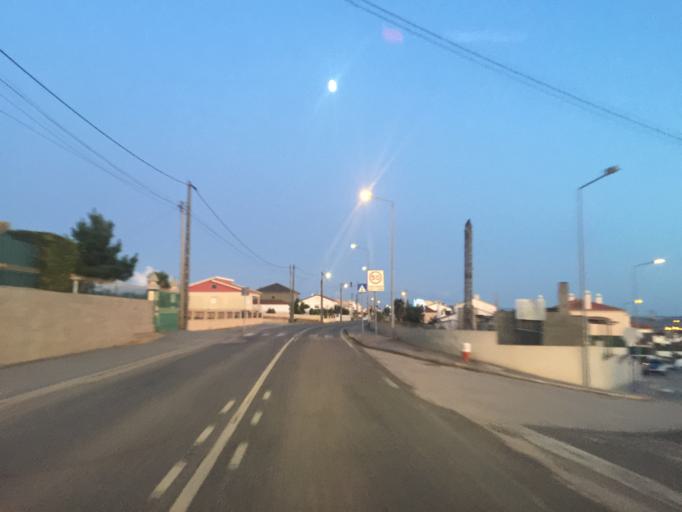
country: PT
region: Lisbon
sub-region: Lourinha
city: Lourinha
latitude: 39.2850
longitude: -9.3033
